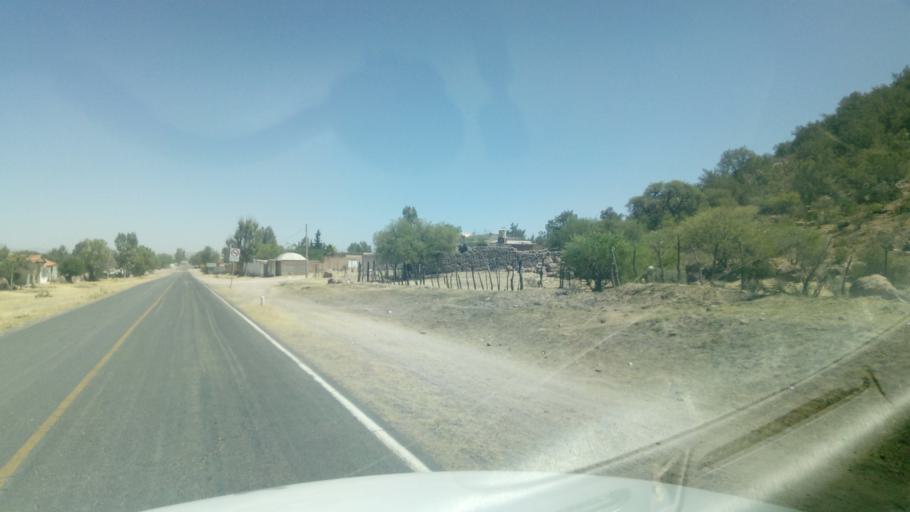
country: MX
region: Durango
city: Victoria de Durango
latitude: 24.1645
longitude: -104.7034
